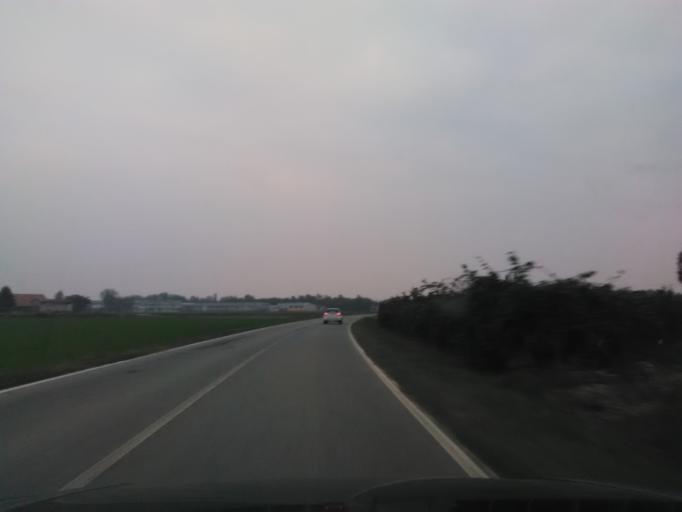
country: IT
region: Piedmont
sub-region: Provincia di Vercelli
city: Santhia
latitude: 45.3718
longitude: 8.1457
